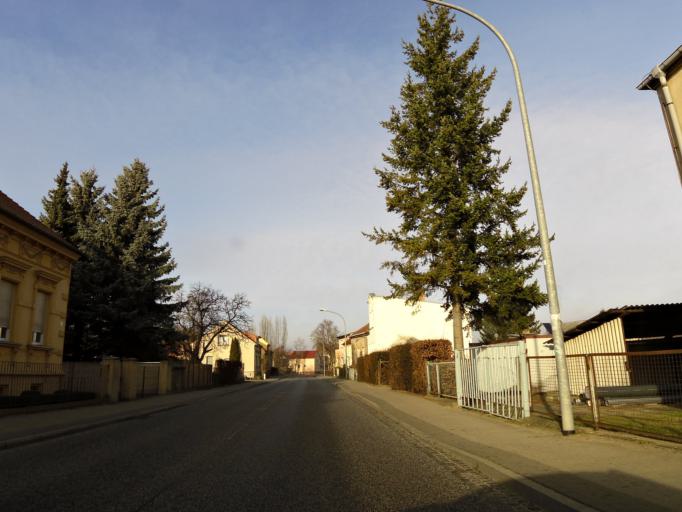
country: DE
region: Brandenburg
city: Werder
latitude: 52.3611
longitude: 12.9092
